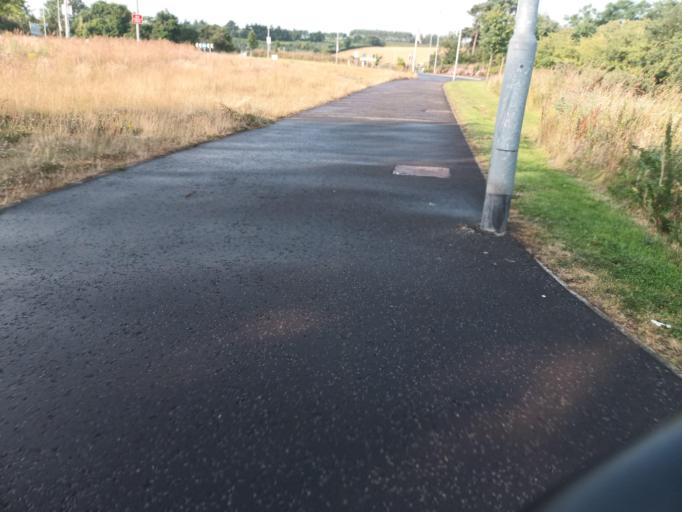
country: GB
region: Northern Ireland
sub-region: Castlereagh District
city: Dundonald
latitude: 54.5833
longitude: -5.7904
